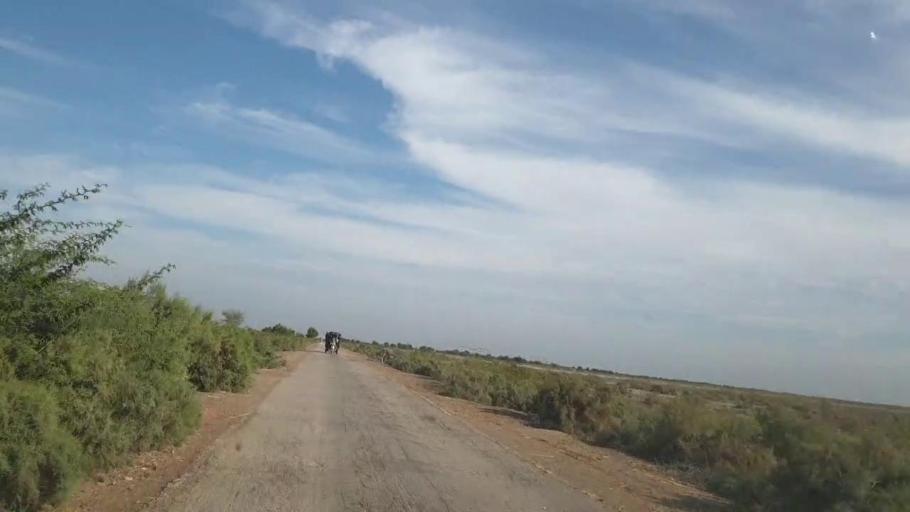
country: PK
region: Sindh
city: Pithoro
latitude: 25.6391
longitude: 69.3816
